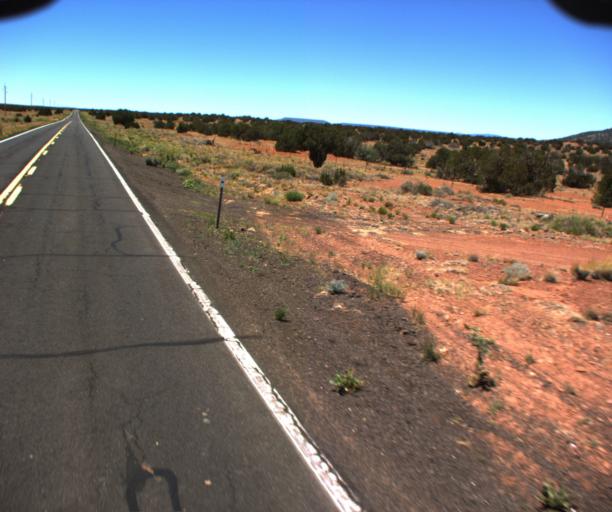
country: US
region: Arizona
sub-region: Coconino County
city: LeChee
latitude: 34.8579
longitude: -110.9187
